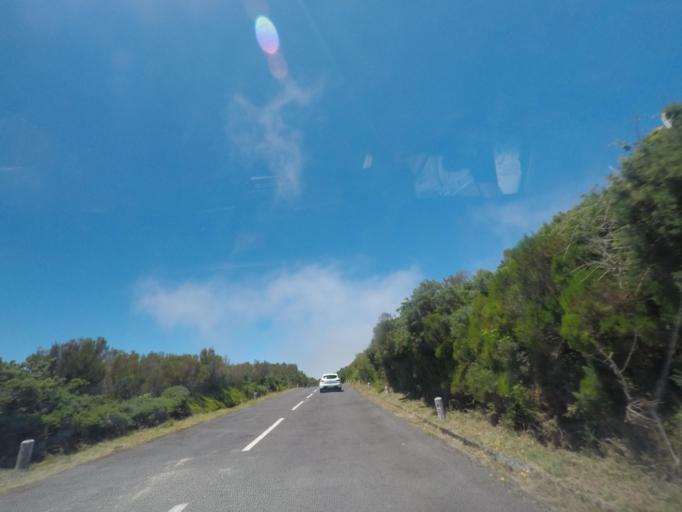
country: PT
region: Madeira
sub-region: Porto Moniz
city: Porto Moniz
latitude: 32.8061
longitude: -17.1921
